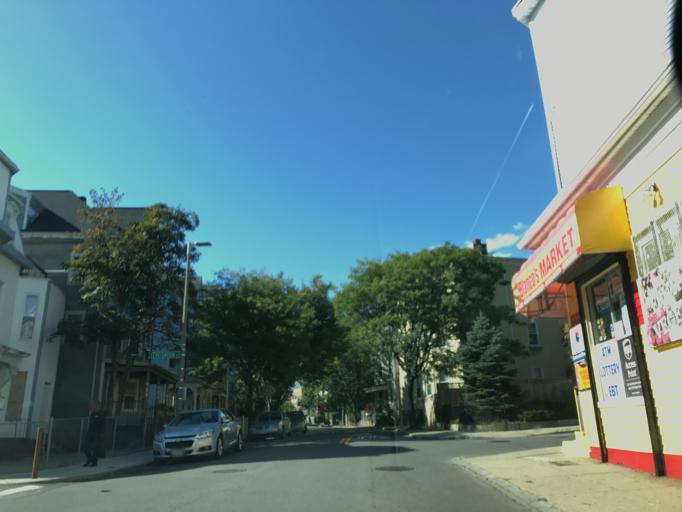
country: US
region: Massachusetts
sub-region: Norfolk County
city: Brookline
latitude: 42.3246
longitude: -71.1081
